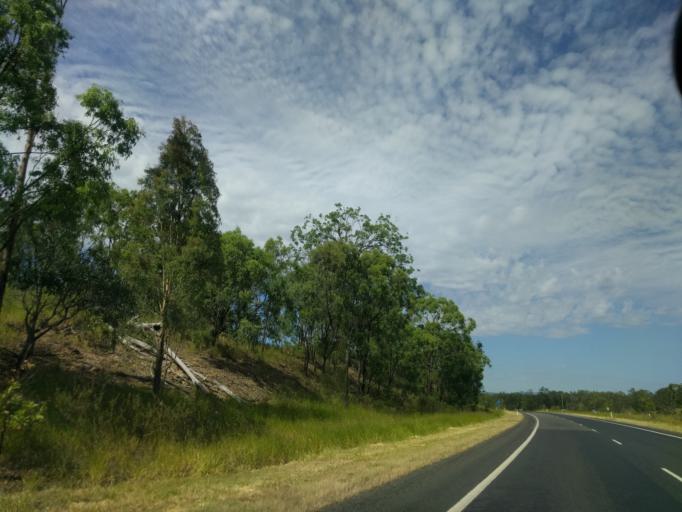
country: AU
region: Queensland
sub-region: Lockyer Valley
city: Gatton
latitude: -27.5353
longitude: 152.2550
